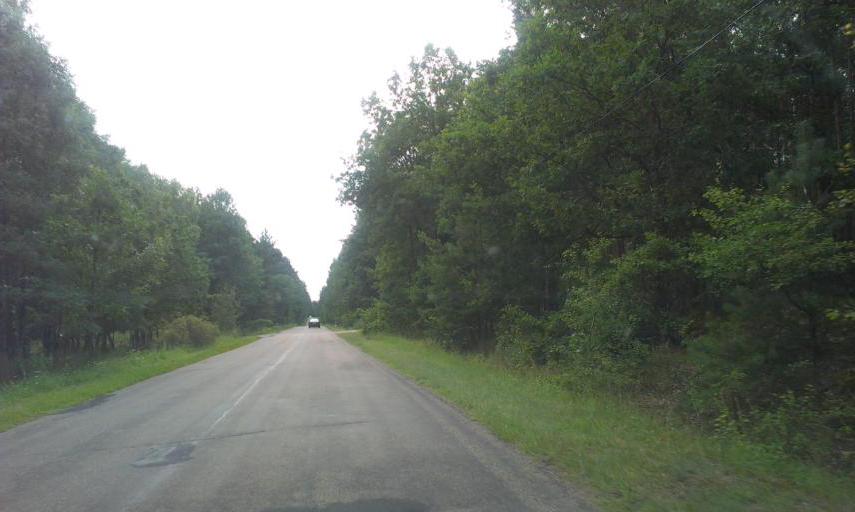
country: PL
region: West Pomeranian Voivodeship
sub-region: Powiat szczecinecki
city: Barwice
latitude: 53.6667
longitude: 16.3386
